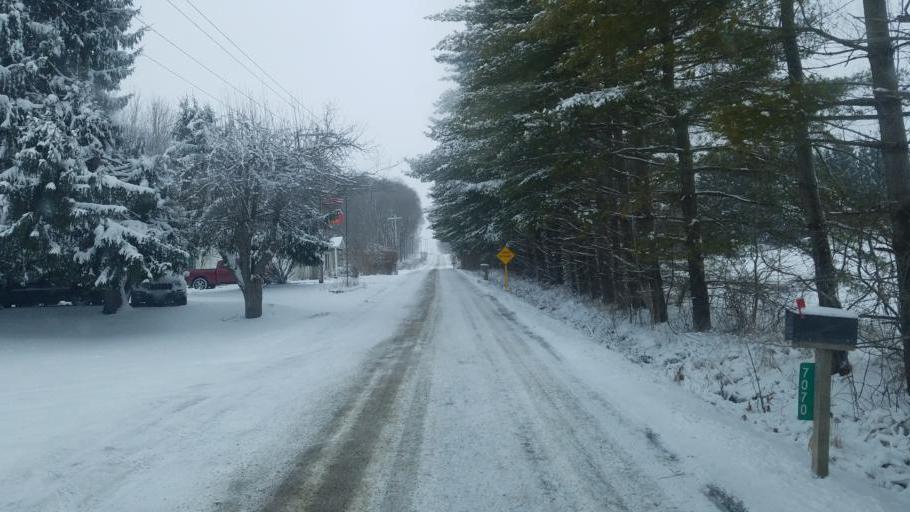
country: US
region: Ohio
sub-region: Knox County
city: Fredericktown
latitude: 40.5207
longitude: -82.6697
